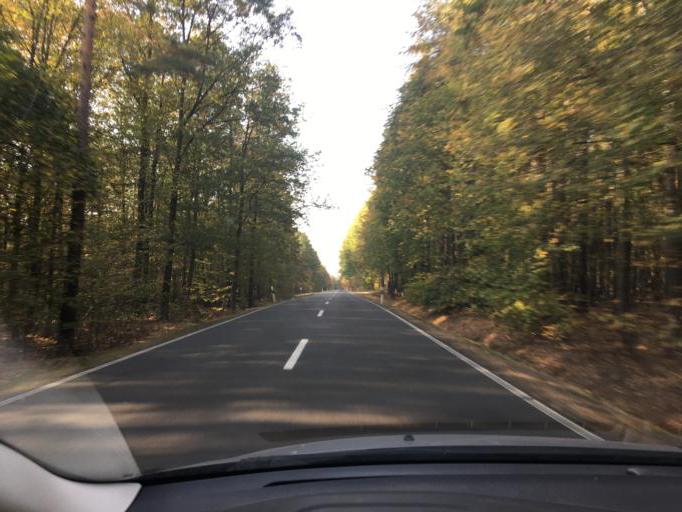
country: DE
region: Saxony
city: Mutzschen
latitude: 51.2922
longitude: 12.9062
